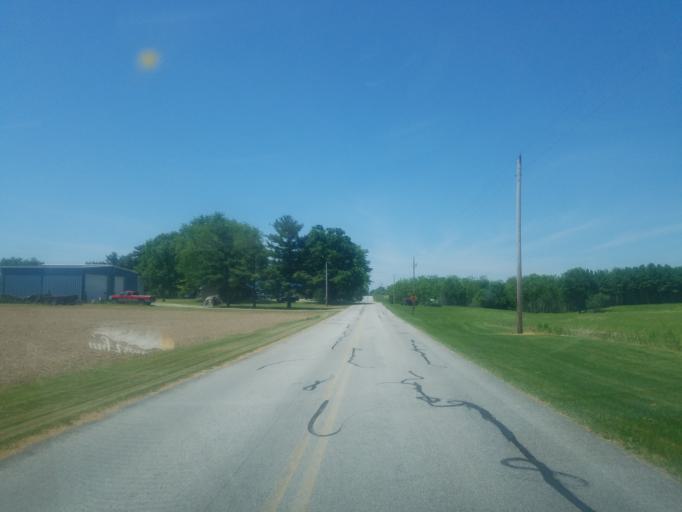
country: US
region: Ohio
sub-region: Huron County
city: New London
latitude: 41.1162
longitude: -82.4062
